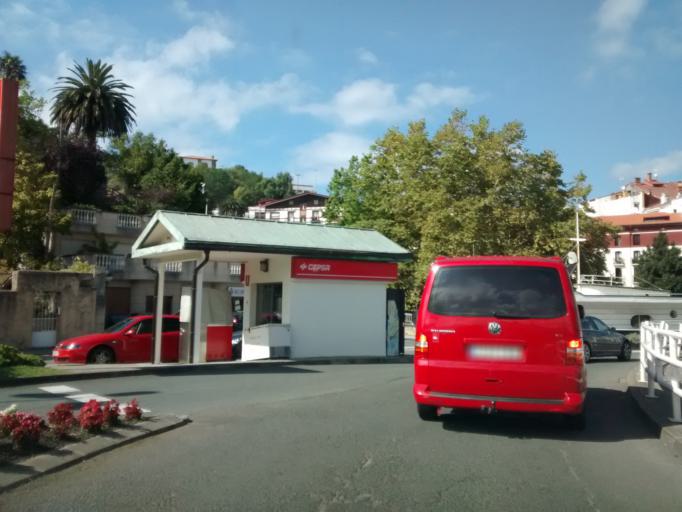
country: ES
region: Basque Country
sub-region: Provincia de Guipuzcoa
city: Zumaia
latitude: 43.2948
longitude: -2.2579
